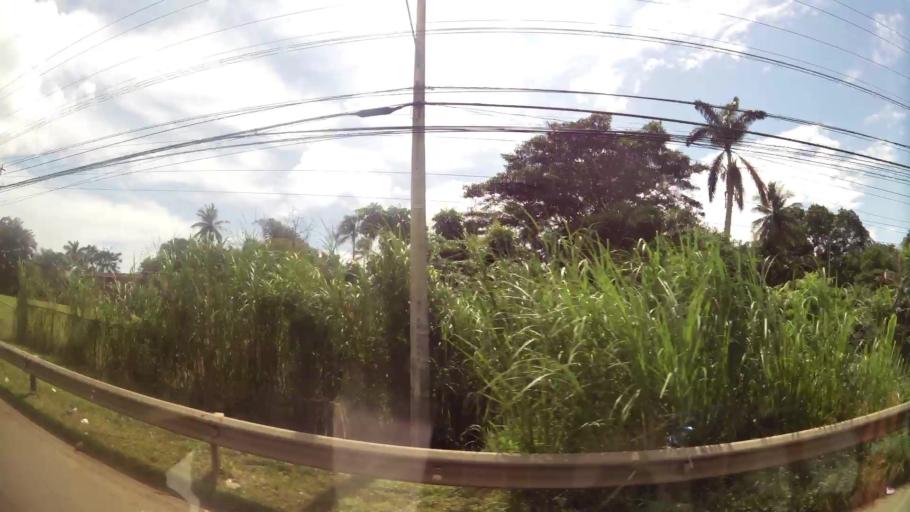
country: PA
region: Panama
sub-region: Distrito Arraijan
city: Arraijan
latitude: 8.9508
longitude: -79.6666
